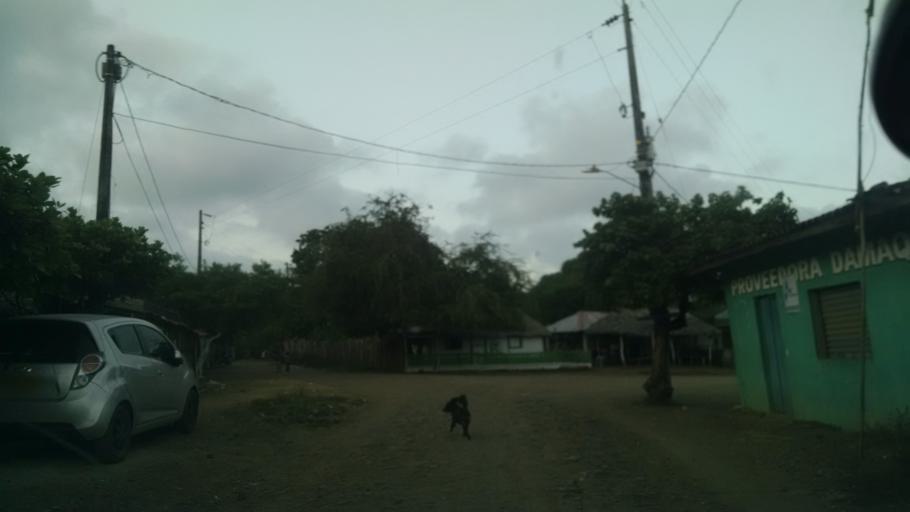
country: CO
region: Antioquia
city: San Juan de Uraba
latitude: 8.7361
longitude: -76.6072
